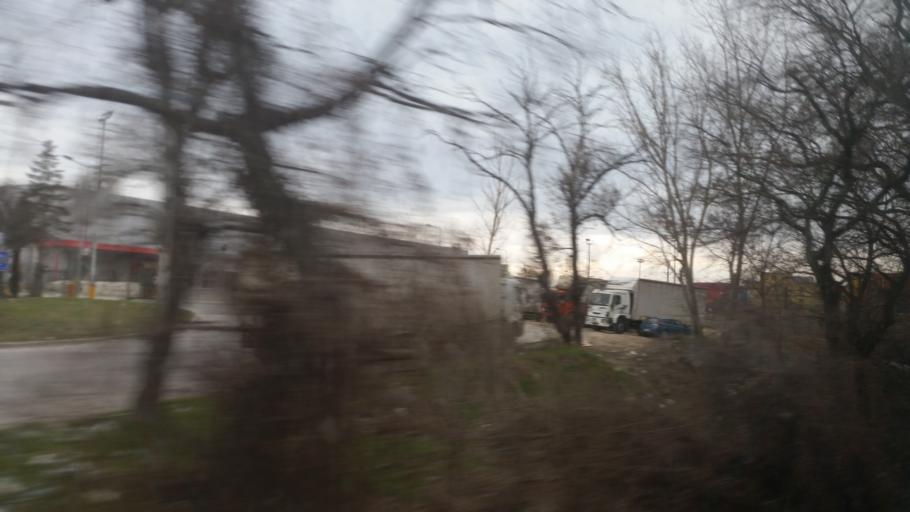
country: TR
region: Tekirdag
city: Cerkezkoey
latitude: 41.2741
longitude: 27.9673
